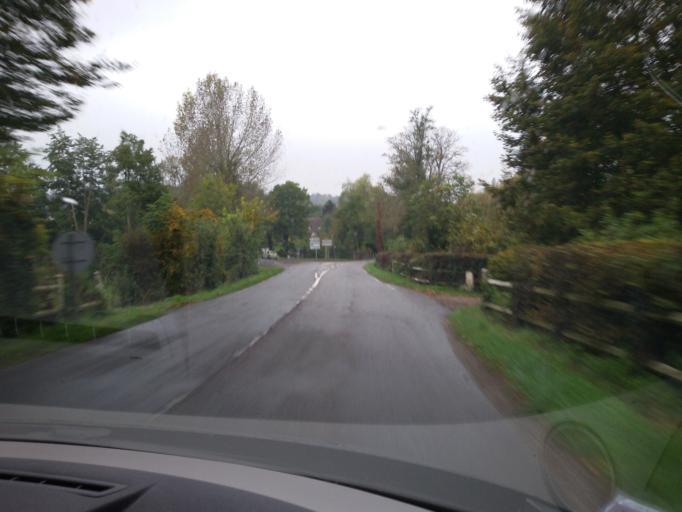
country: FR
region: Lower Normandy
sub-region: Departement du Calvados
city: Equemauville
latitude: 49.4017
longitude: 0.1564
